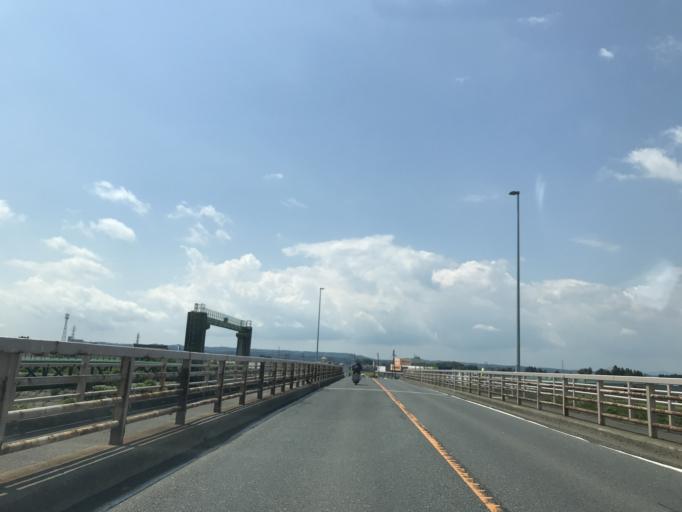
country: JP
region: Miyagi
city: Kogota
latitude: 38.5631
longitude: 141.0453
